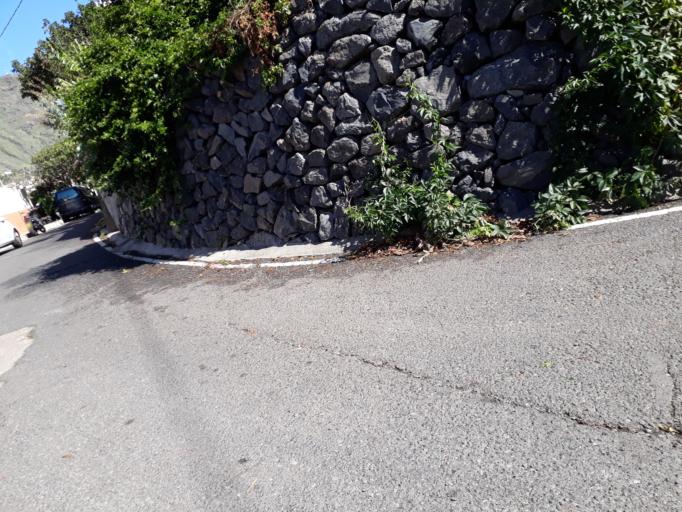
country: ES
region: Canary Islands
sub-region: Provincia de Santa Cruz de Tenerife
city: Vallehermosa
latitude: 28.1088
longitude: -17.3174
